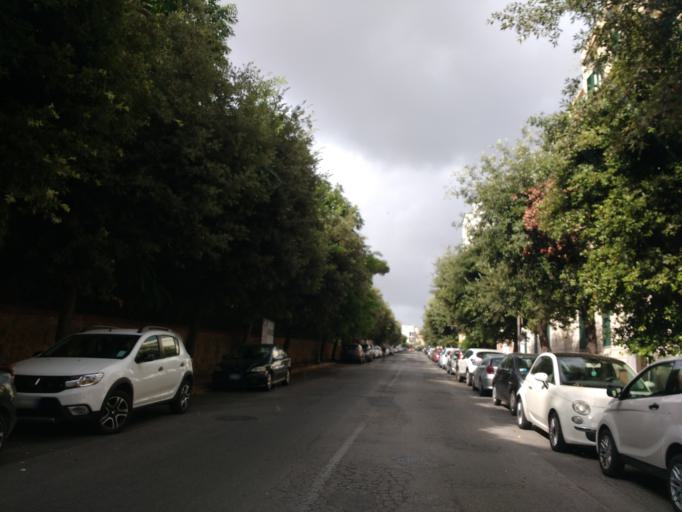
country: IT
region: Latium
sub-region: Citta metropolitana di Roma Capitale
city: Anzio
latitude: 41.4495
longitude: 12.6315
